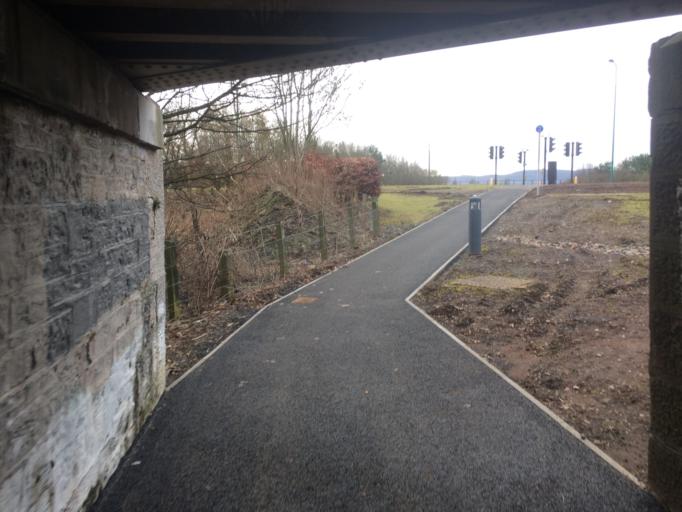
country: GB
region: Scotland
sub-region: Angus
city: Muirhead
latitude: 56.4569
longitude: -3.0353
